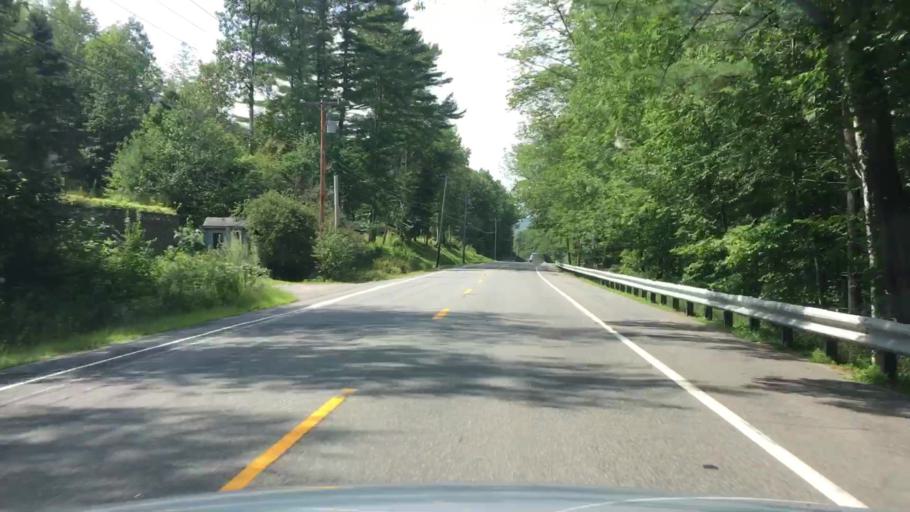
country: US
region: Maine
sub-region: Oxford County
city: Dixfield
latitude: 44.5290
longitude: -70.4832
